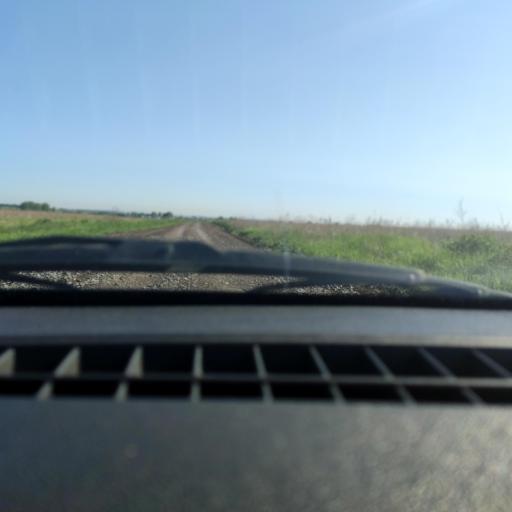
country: RU
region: Bashkortostan
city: Avdon
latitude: 54.5649
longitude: 55.8301
